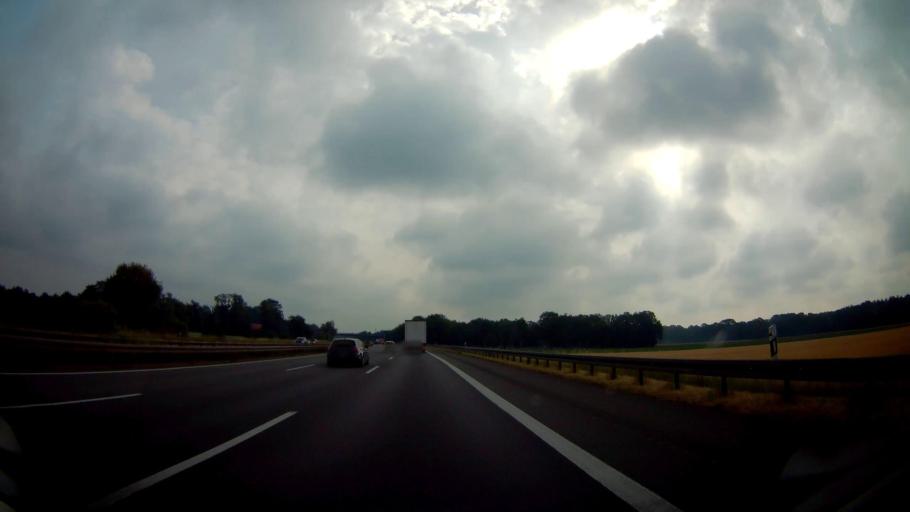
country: DE
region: North Rhine-Westphalia
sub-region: Regierungsbezirk Detmold
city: Guetersloh
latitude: 51.8725
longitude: 8.4136
